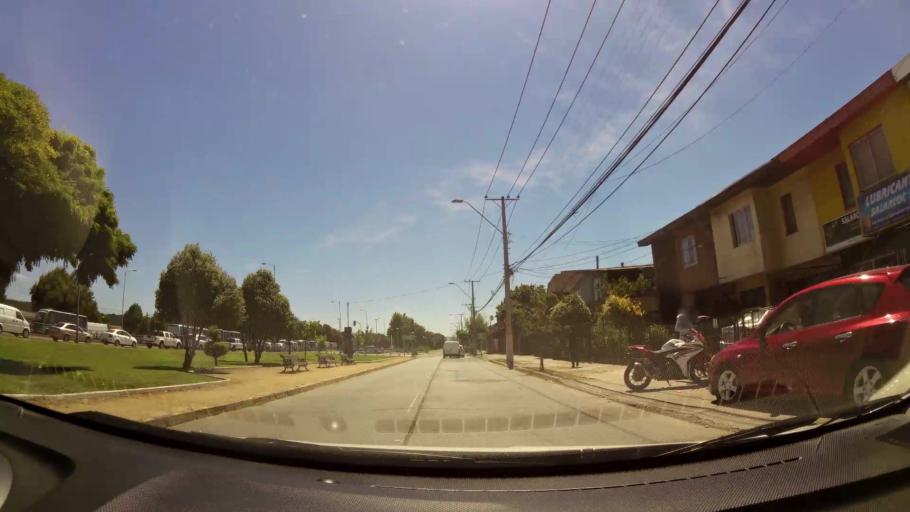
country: CL
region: Biobio
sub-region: Provincia de Concepcion
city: Talcahuano
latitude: -36.7608
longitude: -73.0885
